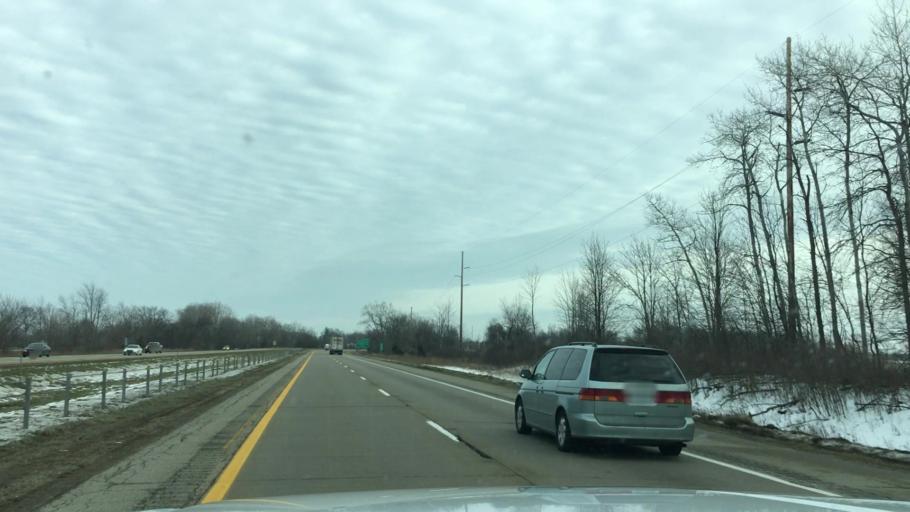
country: US
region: Michigan
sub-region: Ionia County
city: Portland
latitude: 42.8790
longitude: -84.9860
